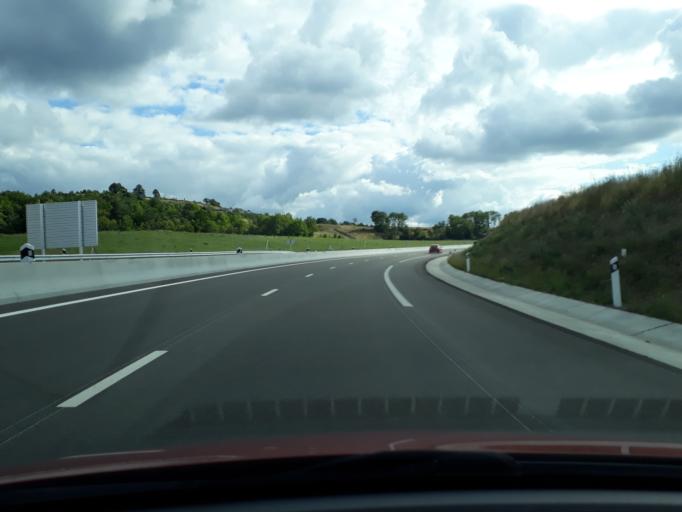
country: FR
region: Auvergne
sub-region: Departement de la Haute-Loire
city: Le Puy-en-Velay
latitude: 45.0302
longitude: 3.9059
